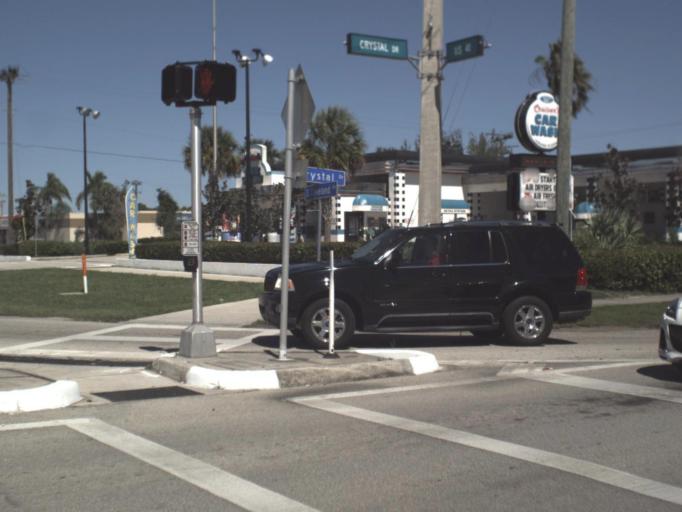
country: US
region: Florida
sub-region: Lee County
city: Pine Manor
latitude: 26.5645
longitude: -81.8718
